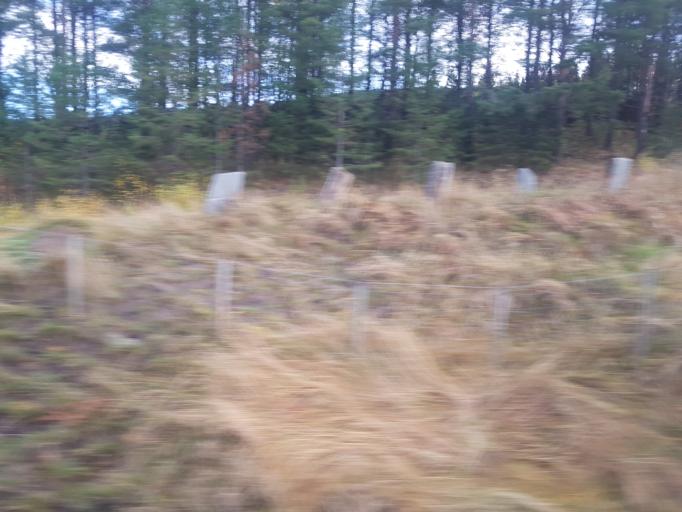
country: NO
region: Oppland
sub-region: Dovre
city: Dovre
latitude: 61.9733
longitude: 9.2574
